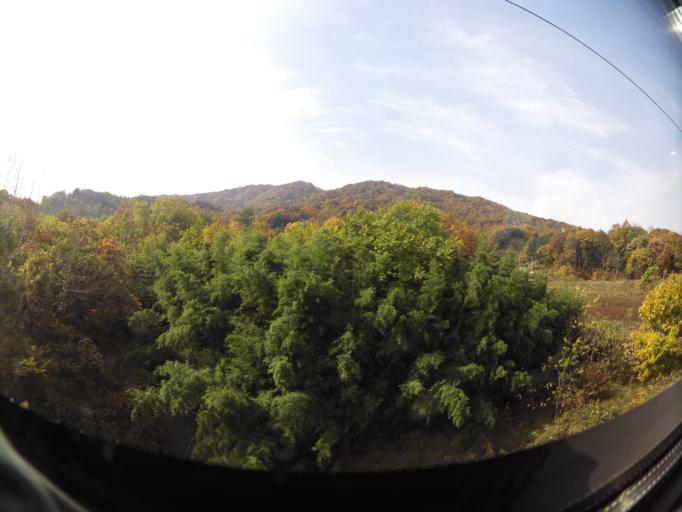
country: KR
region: Gyeongsangbuk-do
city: Gimcheon
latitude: 36.1895
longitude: 128.0068
